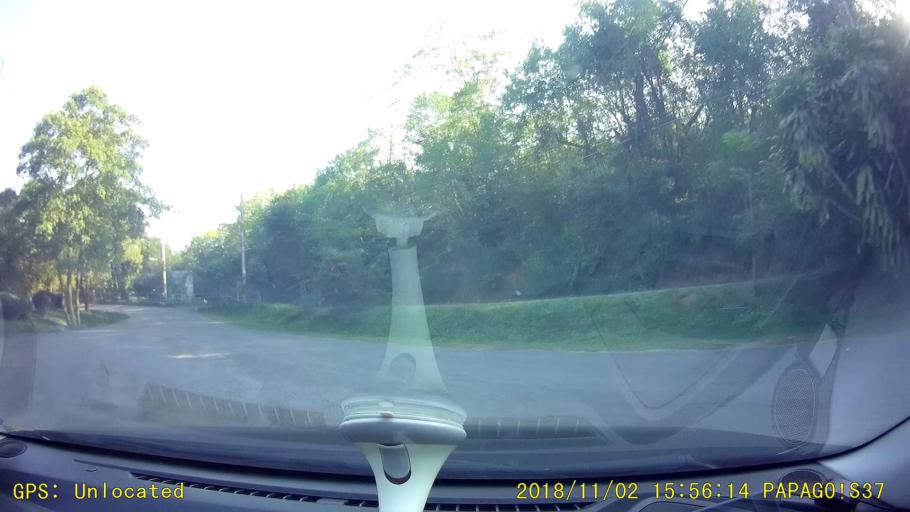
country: TH
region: Nakhon Ratchasima
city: Pak Chong
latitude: 14.7272
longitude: 101.3914
